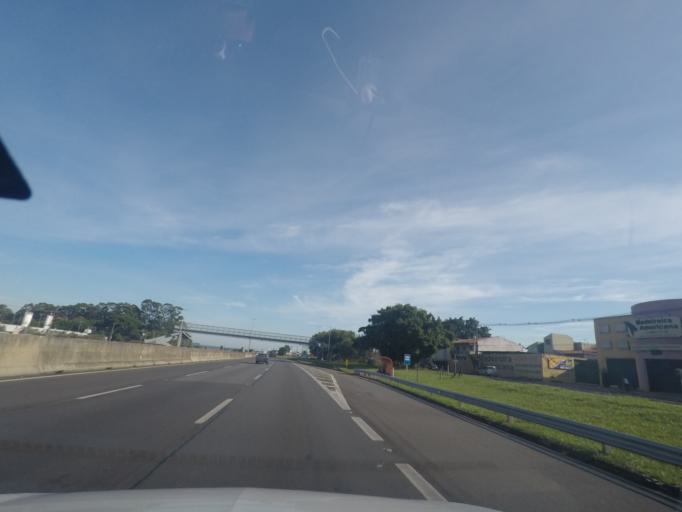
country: BR
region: Sao Paulo
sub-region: Americana
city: Americana
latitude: -22.7139
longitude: -47.2964
